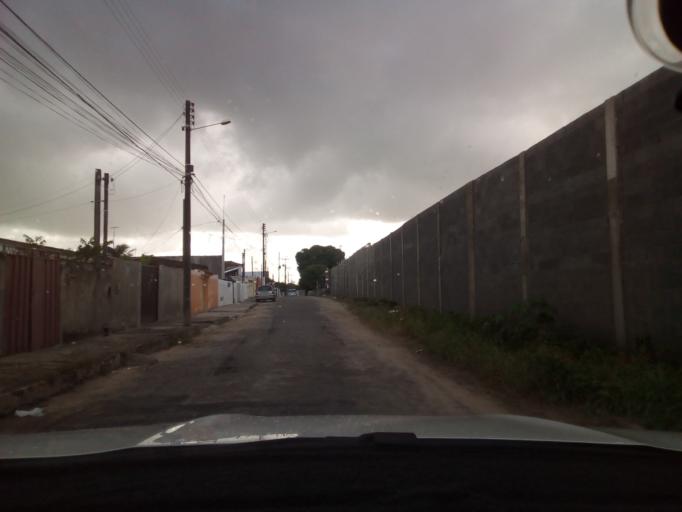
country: BR
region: Paraiba
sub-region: Bayeux
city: Bayeux
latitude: -7.1701
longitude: -34.8919
